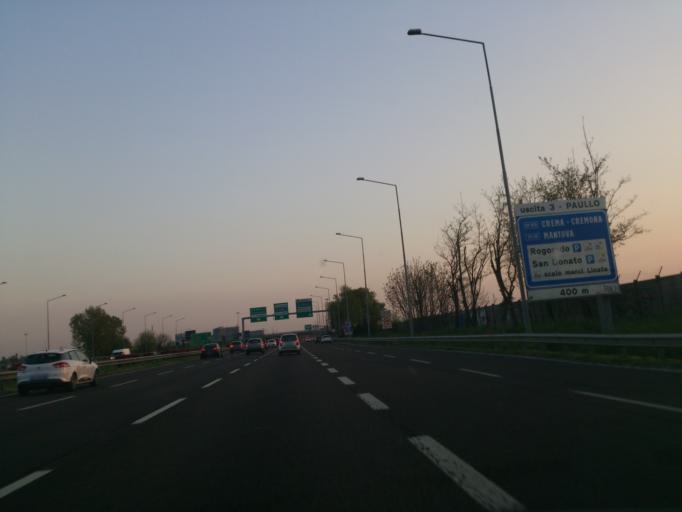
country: IT
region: Lombardy
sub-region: Citta metropolitana di Milano
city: Linate
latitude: 45.4414
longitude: 9.2571
